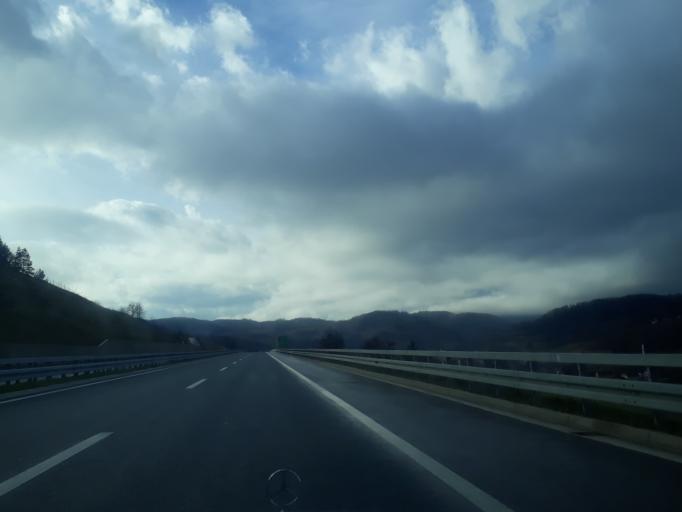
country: BA
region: Federation of Bosnia and Herzegovina
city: Polje
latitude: 43.8513
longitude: 18.1323
